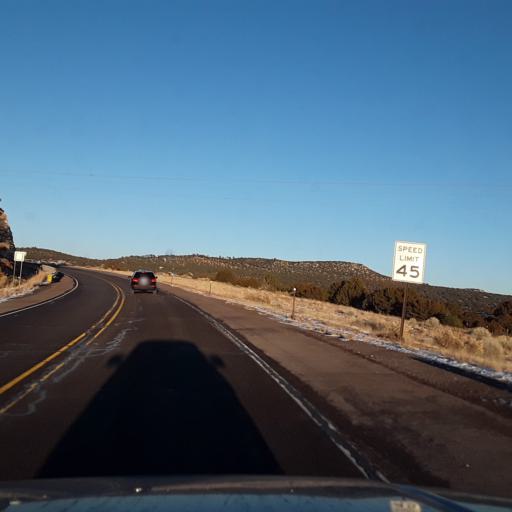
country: US
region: New Mexico
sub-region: Lincoln County
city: Carrizozo
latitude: 34.2401
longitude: -105.5987
